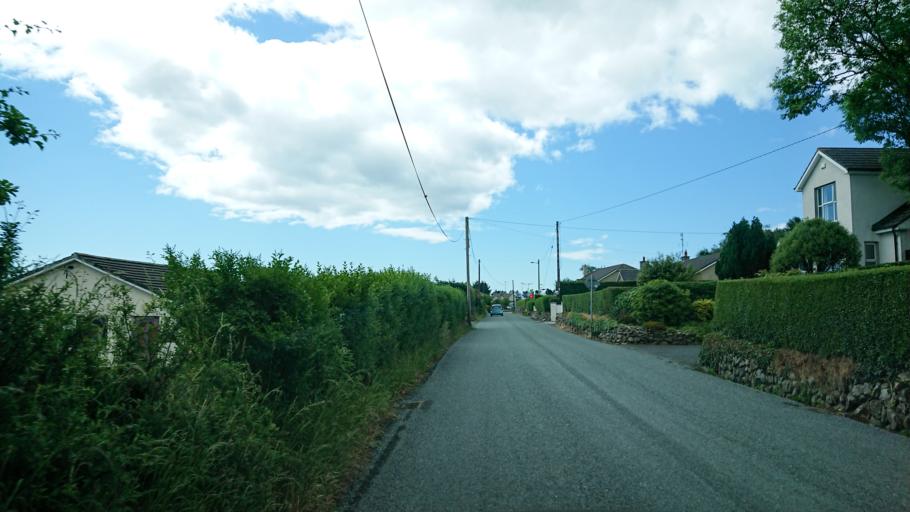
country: IE
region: Munster
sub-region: Waterford
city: Tra Mhor
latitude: 52.1746
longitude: -7.1404
